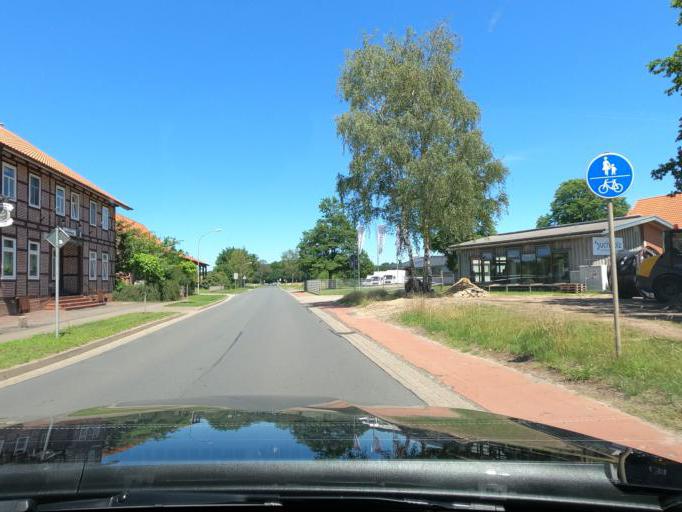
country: DE
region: Lower Saxony
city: Eicklingen
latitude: 52.5604
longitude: 10.1851
